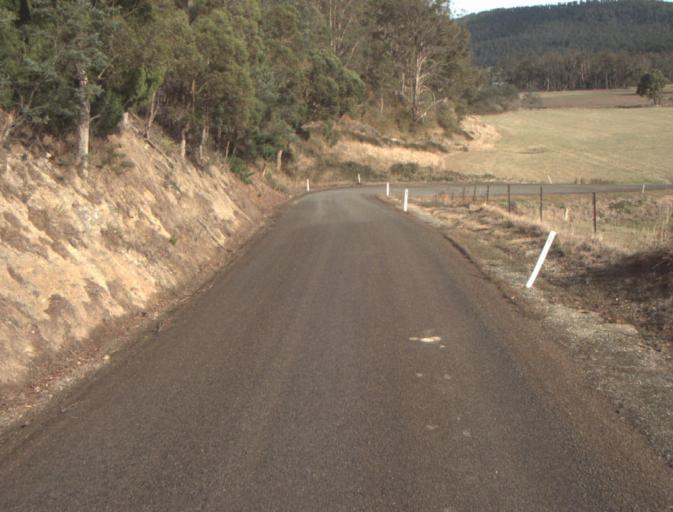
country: AU
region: Tasmania
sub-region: Launceston
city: Mayfield
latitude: -41.2452
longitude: 147.1511
